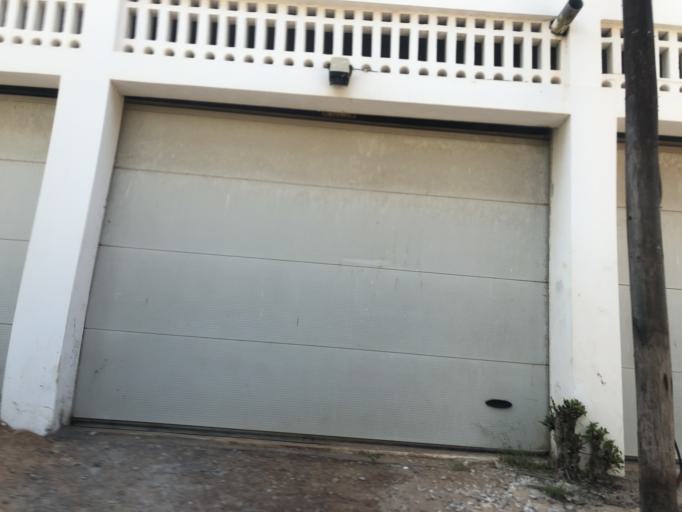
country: SN
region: Dakar
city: Mermoz Boabab
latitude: 14.7597
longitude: -17.4870
